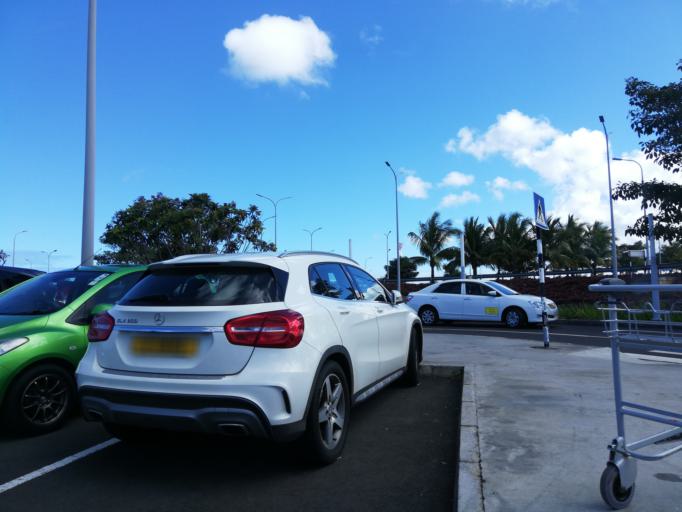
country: MU
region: Grand Port
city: Plaine Magnien
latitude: -20.4340
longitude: 57.6773
